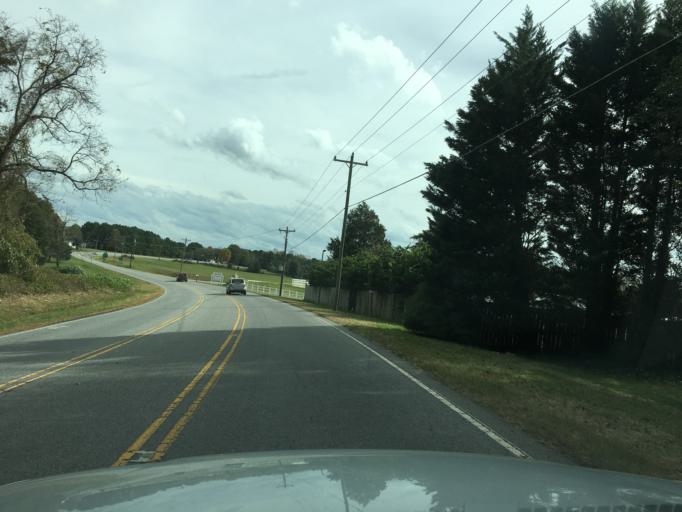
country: US
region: North Carolina
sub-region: Catawba County
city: Newton
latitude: 35.6601
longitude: -81.2714
